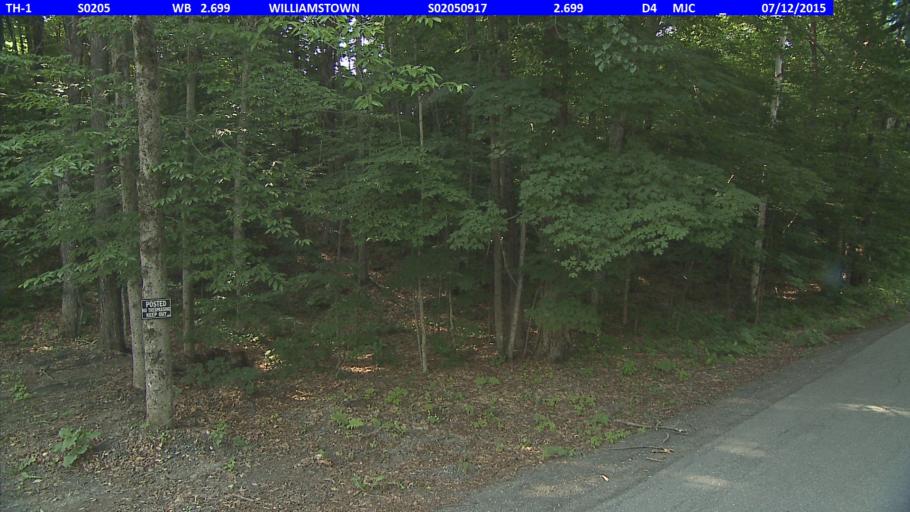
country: US
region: Vermont
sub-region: Orange County
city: Williamstown
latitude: 44.1291
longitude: -72.4947
